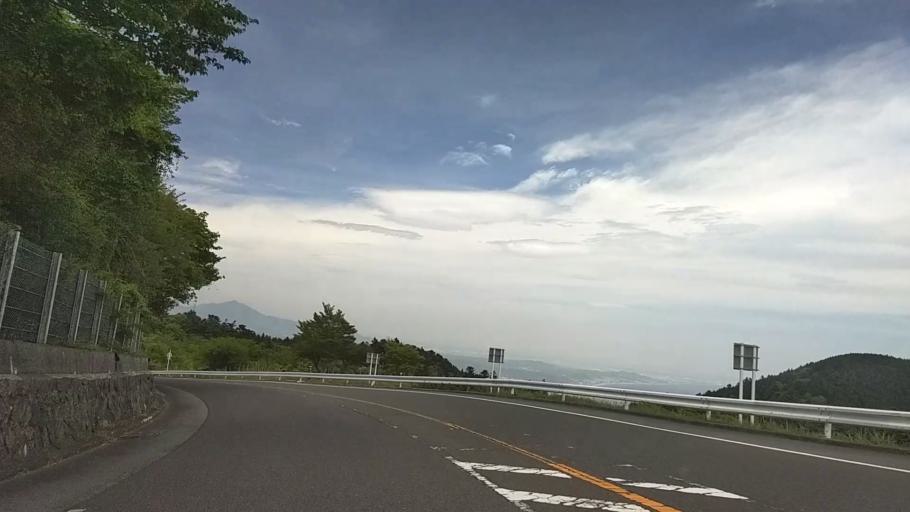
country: JP
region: Kanagawa
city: Yugawara
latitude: 35.2026
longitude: 139.0883
